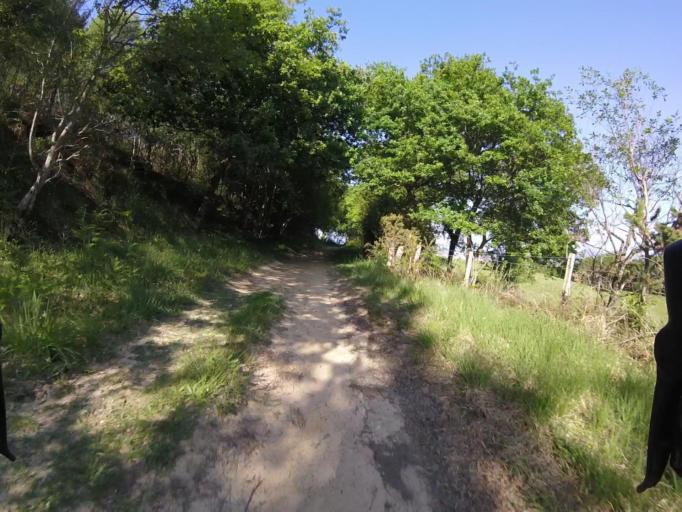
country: ES
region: Basque Country
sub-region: Provincia de Guipuzcoa
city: Fuenterrabia
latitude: 43.3513
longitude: -1.8344
